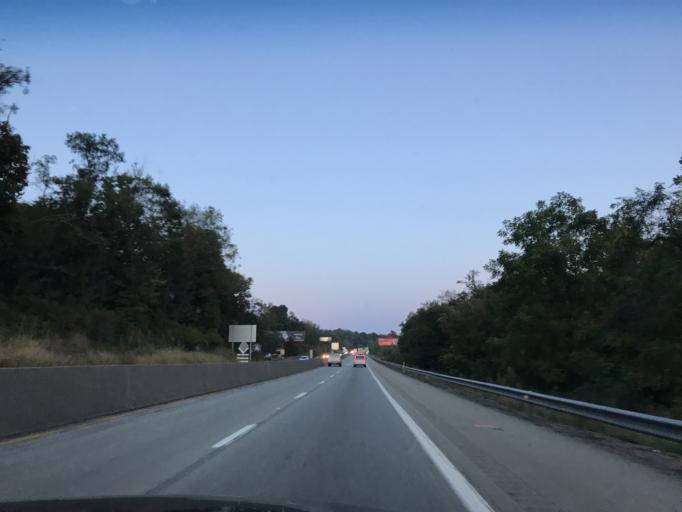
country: US
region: Pennsylvania
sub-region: Washington County
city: Bentleyville
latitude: 40.1304
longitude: -79.9822
